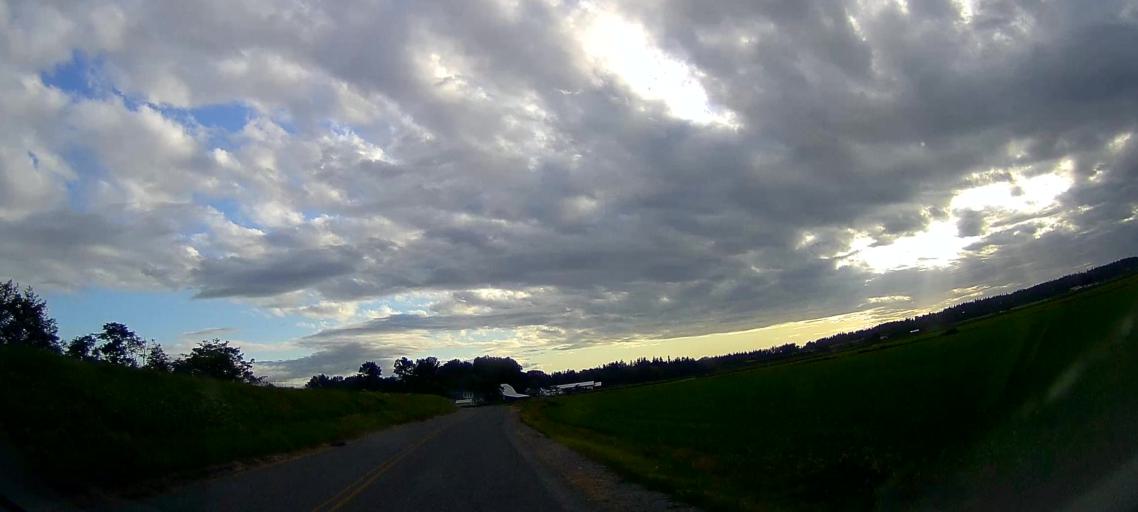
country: US
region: Washington
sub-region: Skagit County
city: Mount Vernon
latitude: 48.3692
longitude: -122.4047
